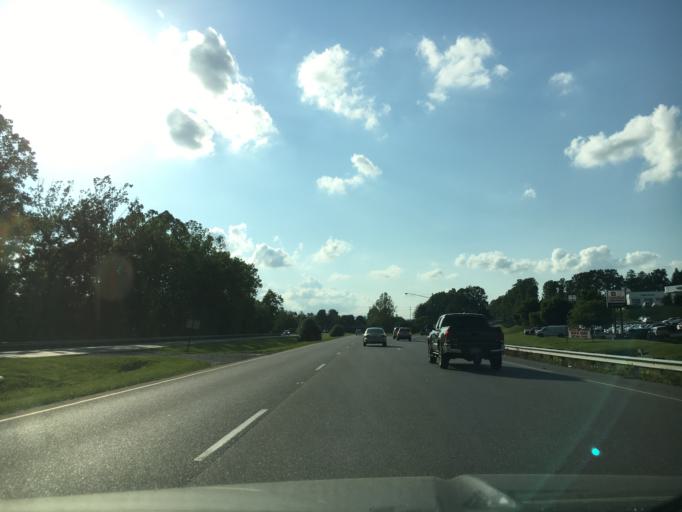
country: US
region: Virginia
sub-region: City of Lynchburg
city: West Lynchburg
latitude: 37.3744
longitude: -79.2157
